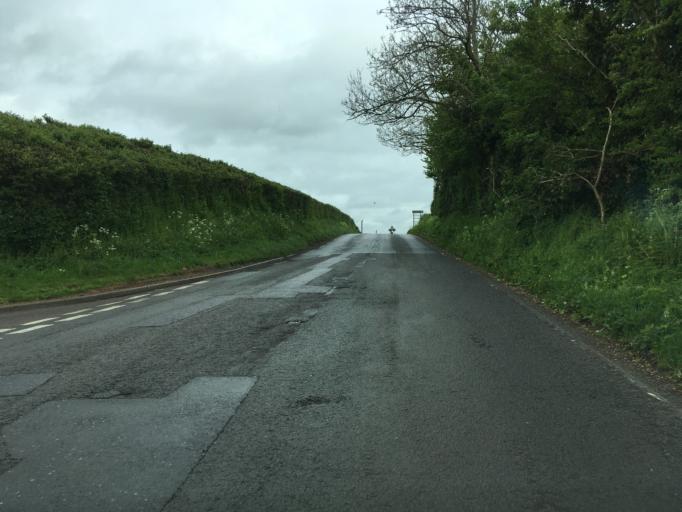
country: GB
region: England
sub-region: Bath and North East Somerset
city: Stanton Drew
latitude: 51.3448
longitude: -2.5773
